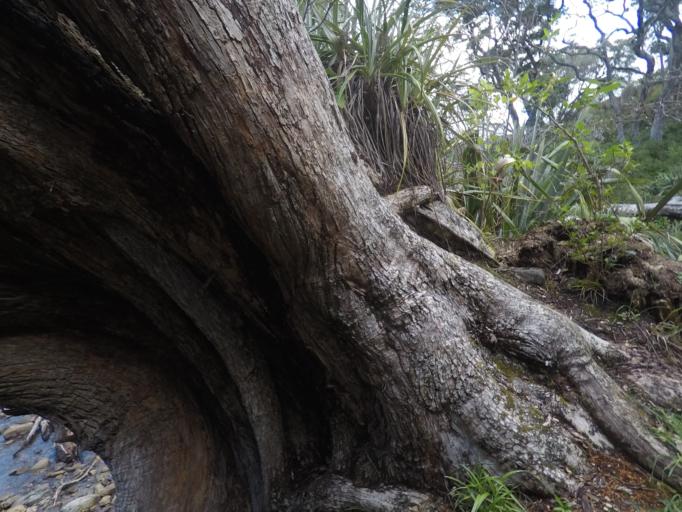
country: NZ
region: Bay of Plenty
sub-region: Western Bay of Plenty District
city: Waihi Beach
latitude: -37.3827
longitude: 175.9372
